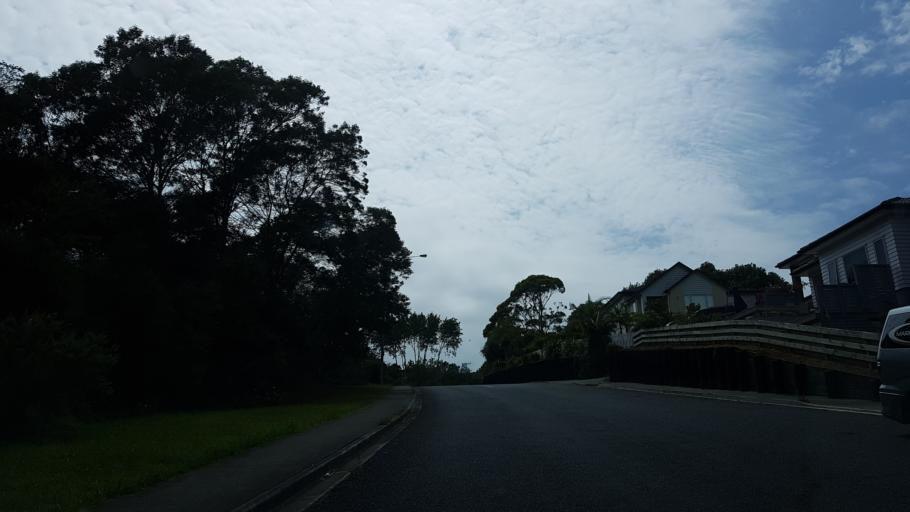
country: NZ
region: Auckland
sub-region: Auckland
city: North Shore
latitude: -36.7690
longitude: 174.7111
